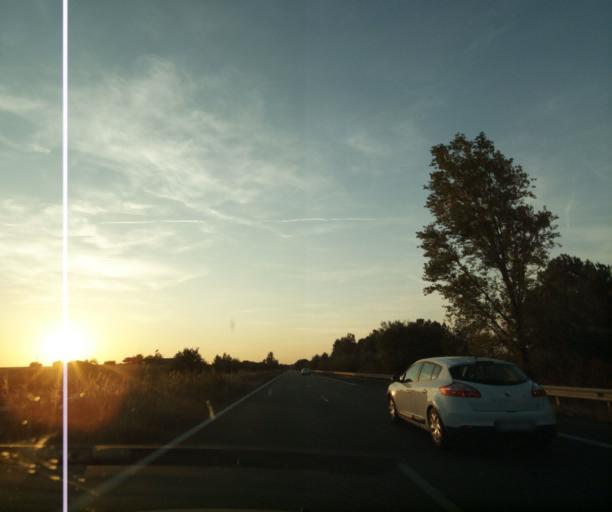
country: FR
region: Aquitaine
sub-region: Departement du Lot-et-Garonne
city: Fourques-sur-Garonne
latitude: 44.4461
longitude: 0.1025
